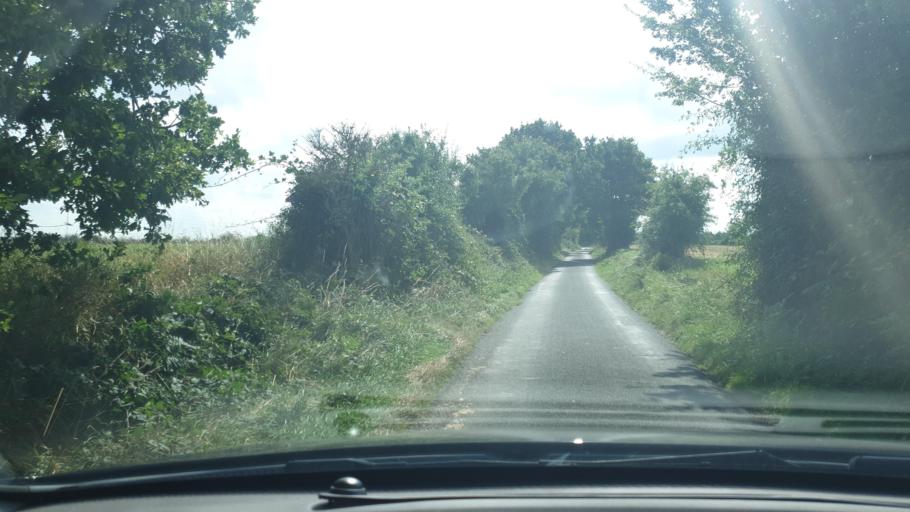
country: GB
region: England
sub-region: Essex
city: Manningtree
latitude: 51.9271
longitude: 1.0300
